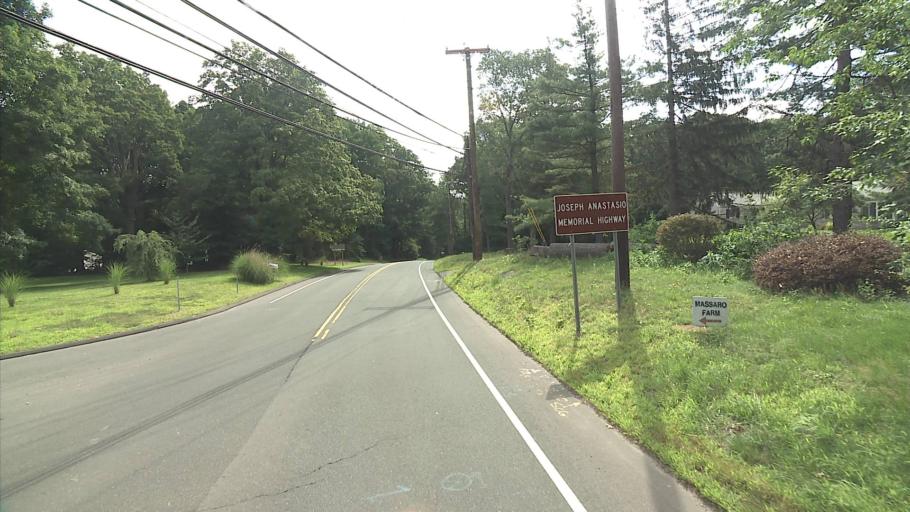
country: US
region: Connecticut
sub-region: New Haven County
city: Woodbridge
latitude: 41.3324
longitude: -73.0401
